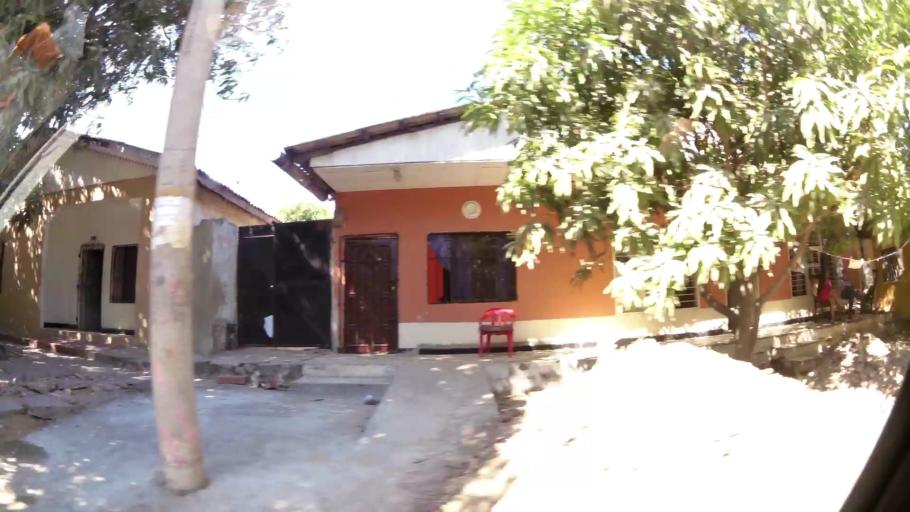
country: CO
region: Atlantico
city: Barranquilla
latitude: 10.9946
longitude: -74.7858
